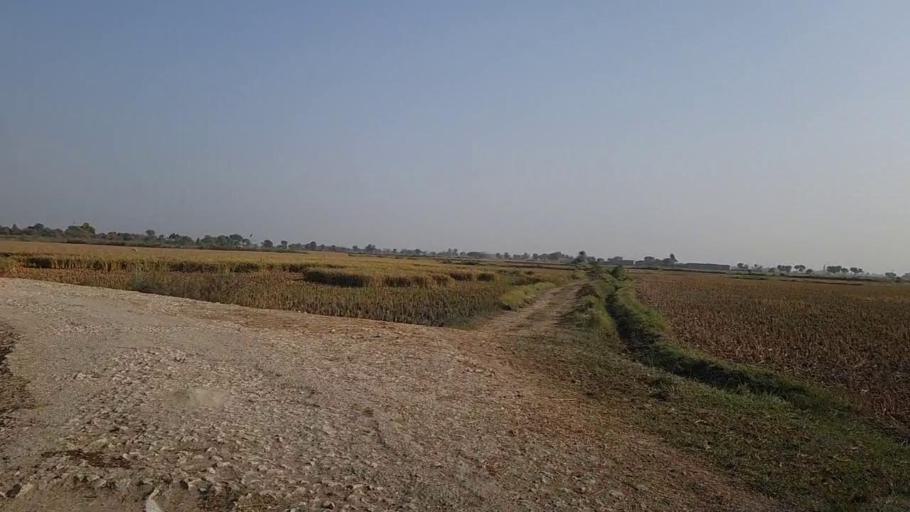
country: PK
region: Sindh
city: Kandhkot
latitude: 28.2899
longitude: 69.2535
